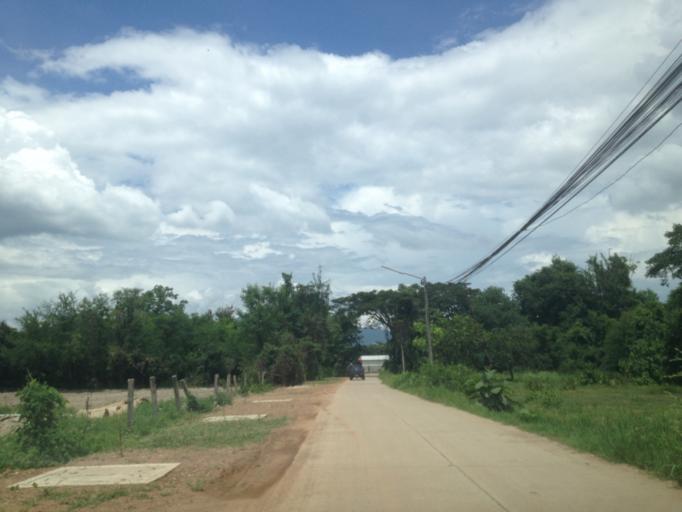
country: TH
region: Chiang Mai
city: Hang Dong
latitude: 18.6833
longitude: 98.9054
